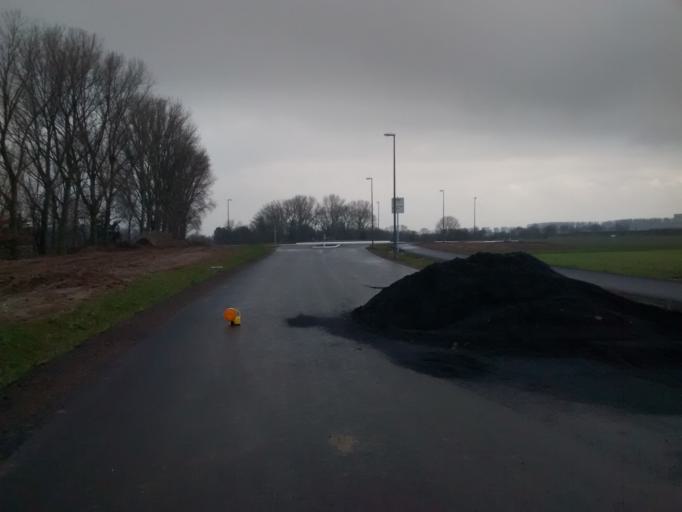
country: DE
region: North Rhine-Westphalia
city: Monheim am Rhein
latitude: 51.0403
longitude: 6.9090
